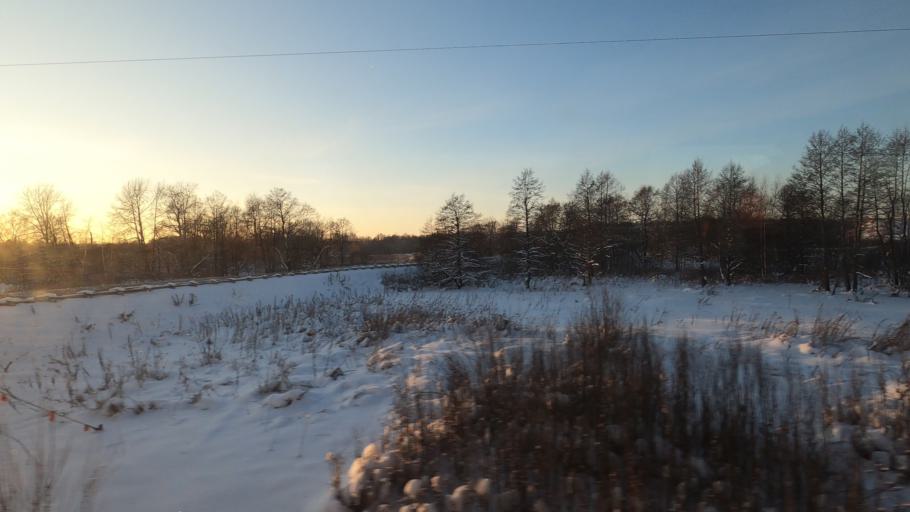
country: RU
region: Moskovskaya
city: Orud'yevo
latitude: 56.4030
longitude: 37.4938
